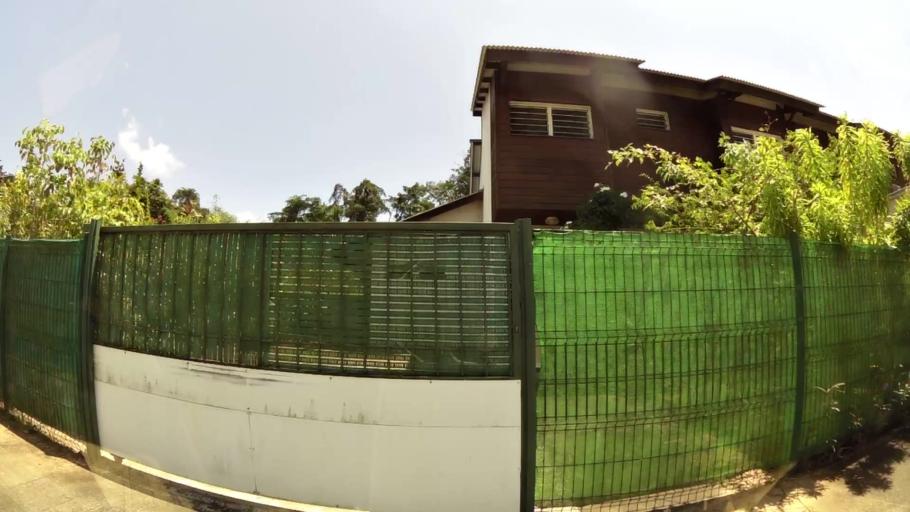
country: GF
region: Guyane
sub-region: Guyane
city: Cayenne
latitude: 4.9015
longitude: -52.3390
